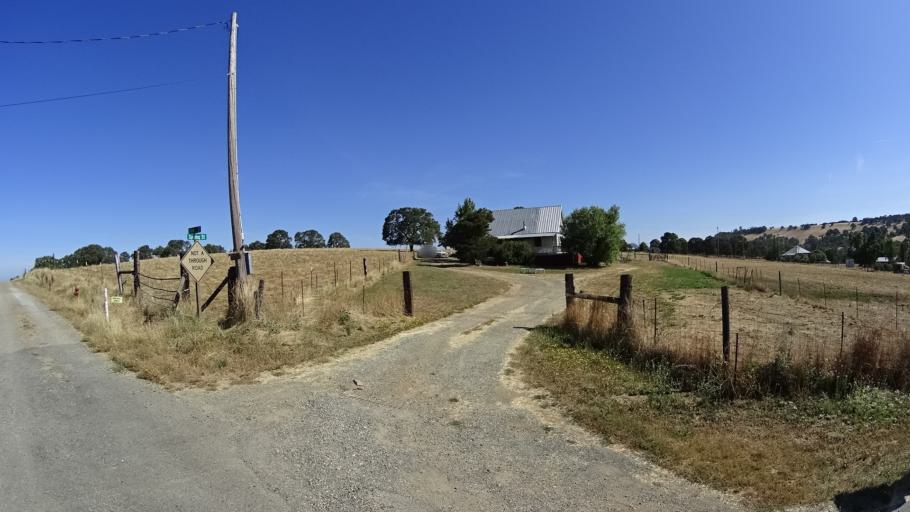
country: US
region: California
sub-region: Amador County
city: Jackson
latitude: 38.2602
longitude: -120.7650
